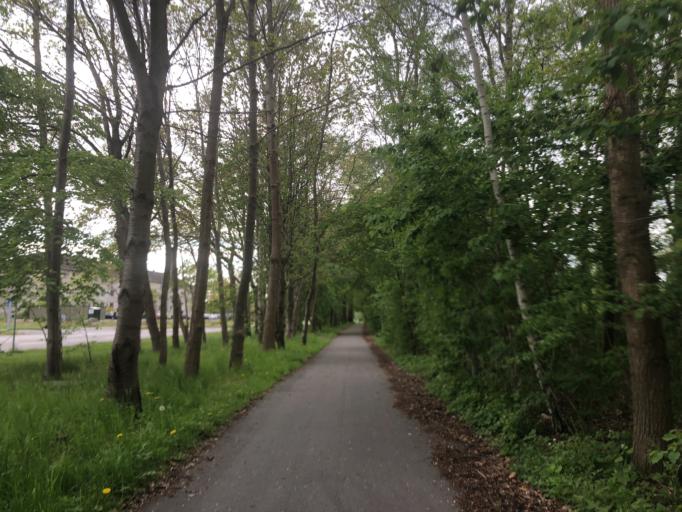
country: DK
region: Zealand
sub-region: Koge Kommune
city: Koge
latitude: 55.4482
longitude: 12.1645
